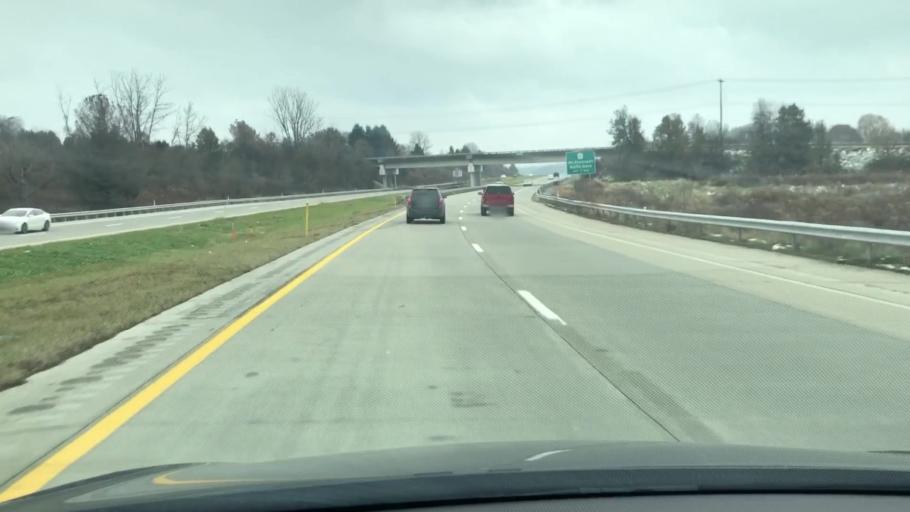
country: US
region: Pennsylvania
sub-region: Westmoreland County
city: Mount Pleasant
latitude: 40.1725
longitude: -79.5600
